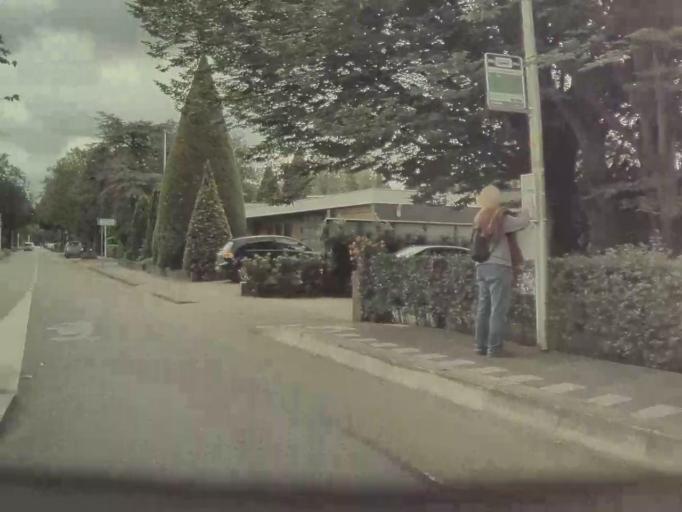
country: NL
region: South Holland
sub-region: Gemeente Voorschoten
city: Voorschoten
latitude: 52.1208
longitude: 4.4329
